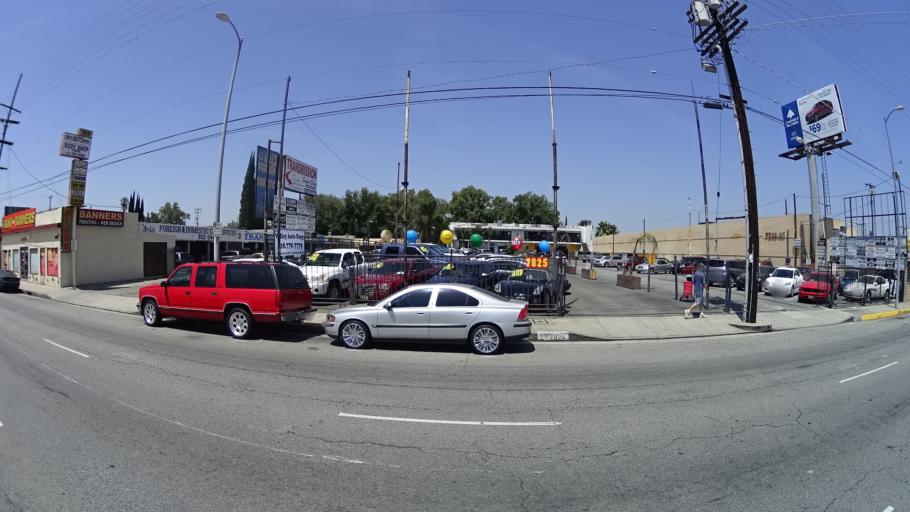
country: US
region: California
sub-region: Los Angeles County
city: Van Nuys
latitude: 34.2129
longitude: -118.4663
